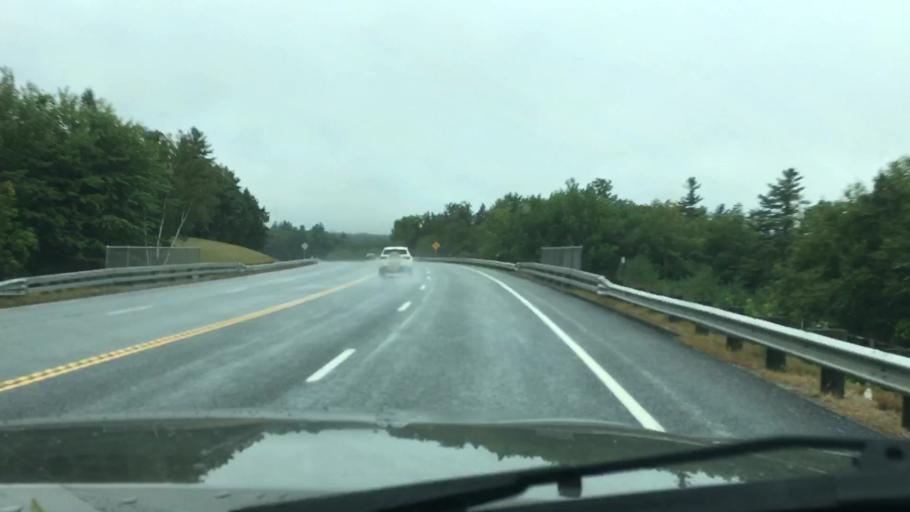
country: US
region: New Hampshire
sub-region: Cheshire County
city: Harrisville
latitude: 43.0135
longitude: -72.1407
